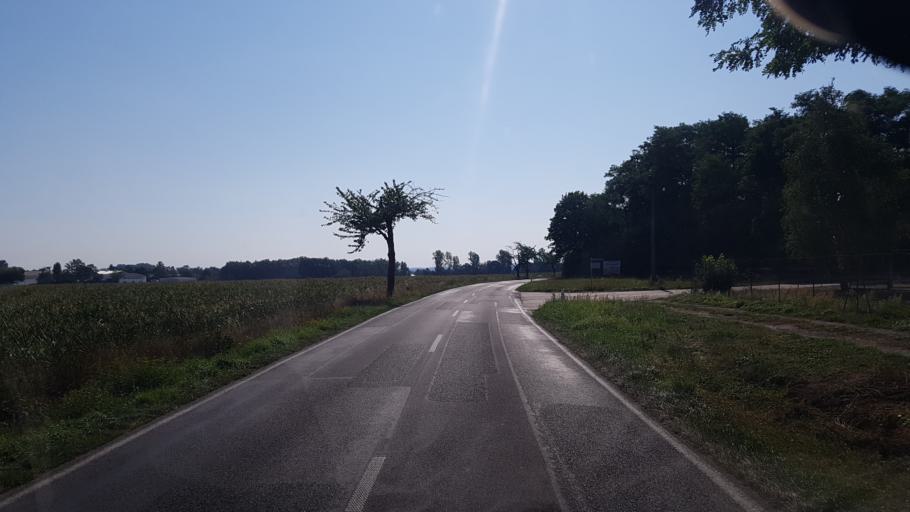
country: DE
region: Brandenburg
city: Hirschfeld
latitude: 51.3946
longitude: 13.6032
